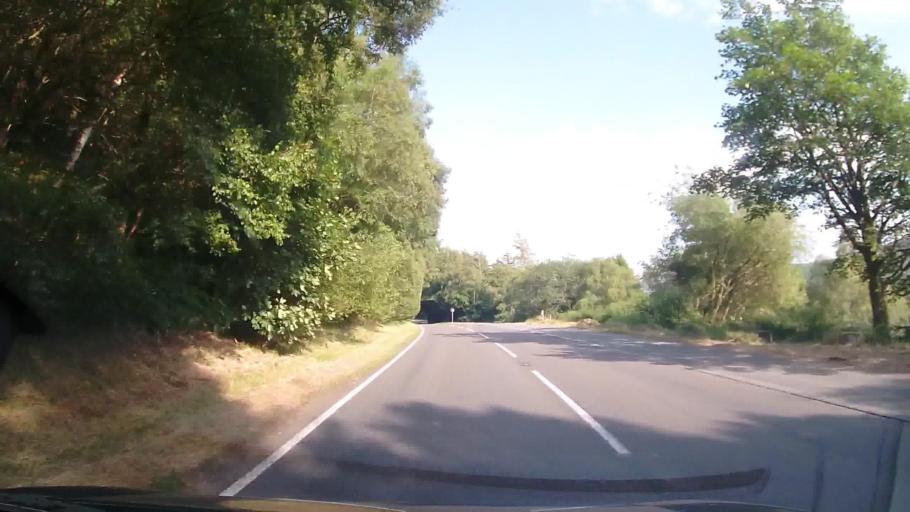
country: GB
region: Wales
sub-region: Gwynedd
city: Bala
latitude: 52.9533
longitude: -3.6909
